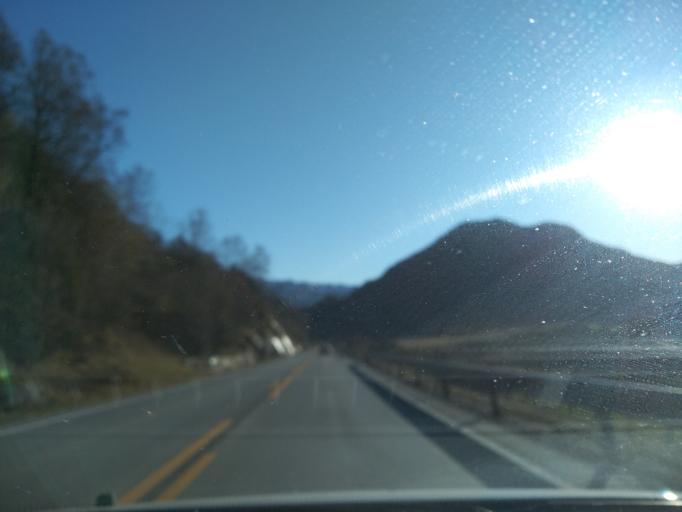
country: NO
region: Hordaland
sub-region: Etne
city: Etne
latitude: 59.7476
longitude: 6.1241
